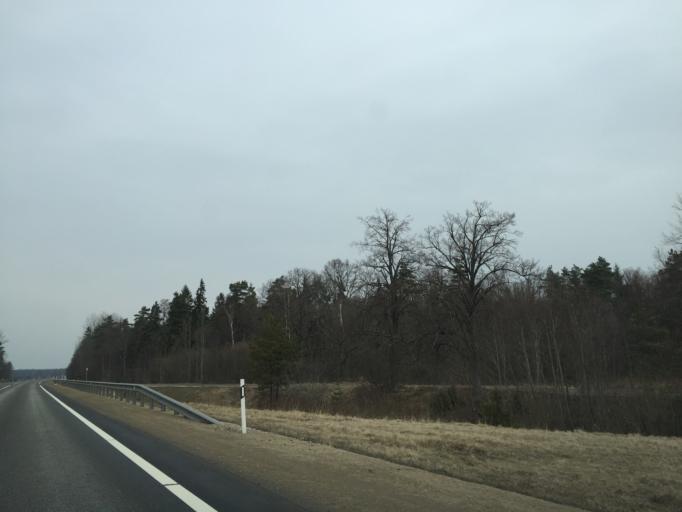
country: LV
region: Salacgrivas
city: Salacgriva
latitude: 57.7105
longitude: 24.3671
